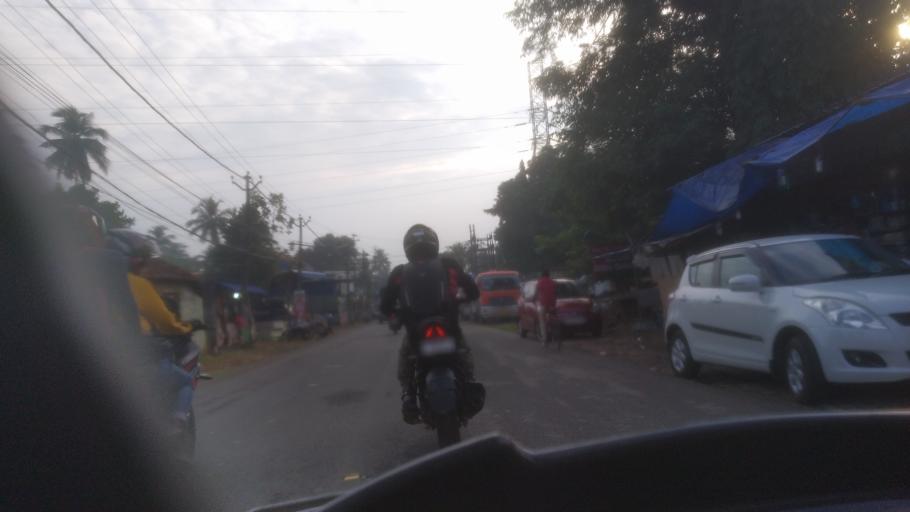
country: IN
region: Kerala
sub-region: Ernakulam
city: Perumpavur
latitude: 10.1162
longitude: 76.4580
